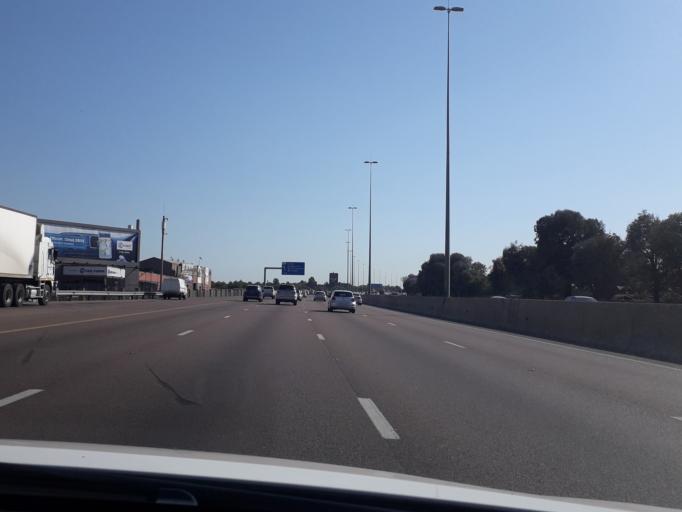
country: ZA
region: Gauteng
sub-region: City of Tshwane Metropolitan Municipality
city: Centurion
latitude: -25.8432
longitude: 28.2310
